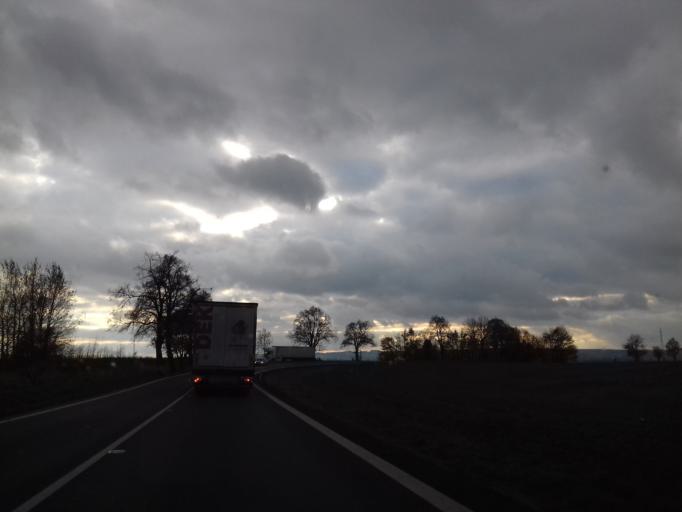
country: CZ
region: Pardubicky
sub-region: Okres Svitavy
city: Svitavy
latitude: 49.7609
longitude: 16.5101
